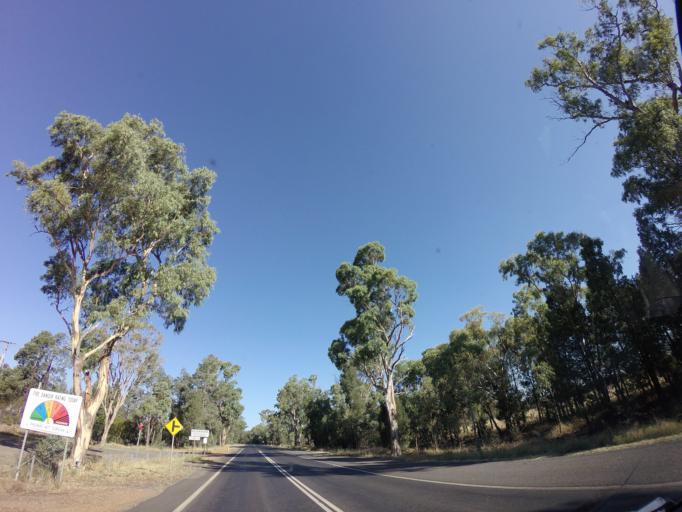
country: AU
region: New South Wales
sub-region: Gilgandra
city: Gilgandra
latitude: -31.7072
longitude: 148.6355
